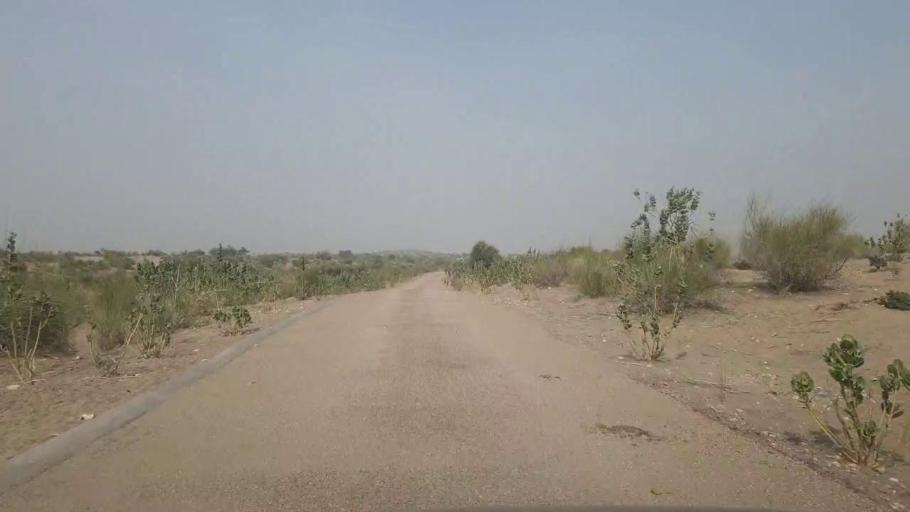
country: PK
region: Sindh
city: Chor
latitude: 25.6034
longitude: 69.9901
